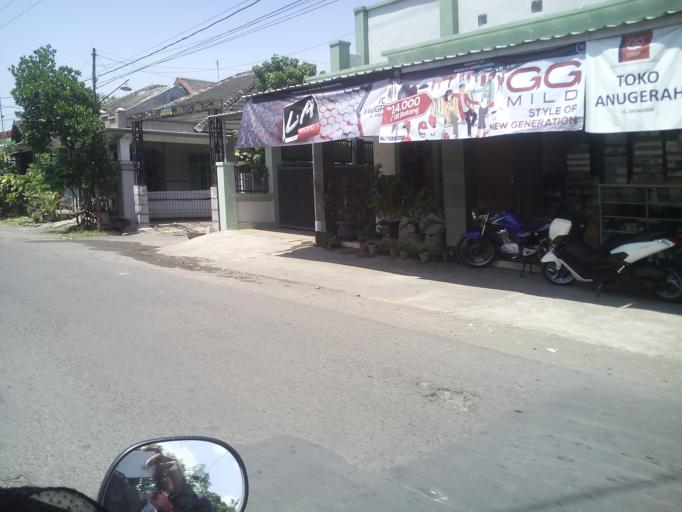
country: ID
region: East Java
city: Kloncing
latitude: -8.1824
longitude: 113.7202
